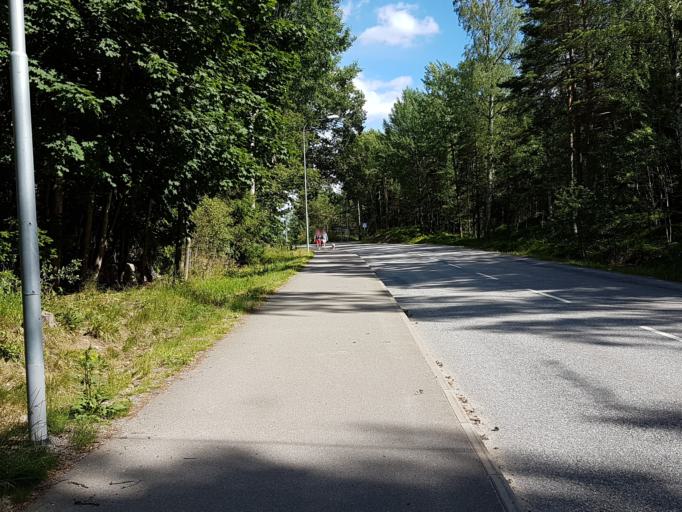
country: SE
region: Stockholm
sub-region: Nacka Kommun
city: Kummelnas
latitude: 59.3440
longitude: 18.2492
